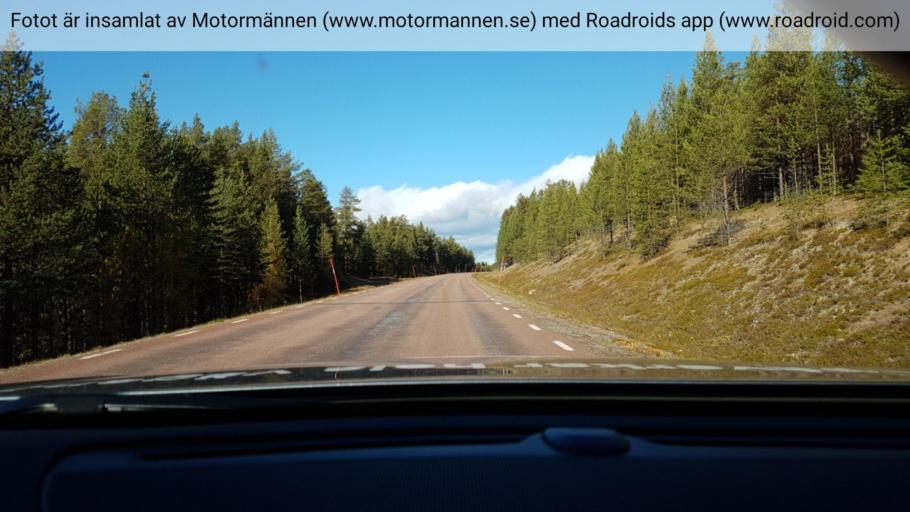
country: SE
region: Norrbotten
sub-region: Arjeplogs Kommun
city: Arjeplog
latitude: 66.0185
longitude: 18.0761
